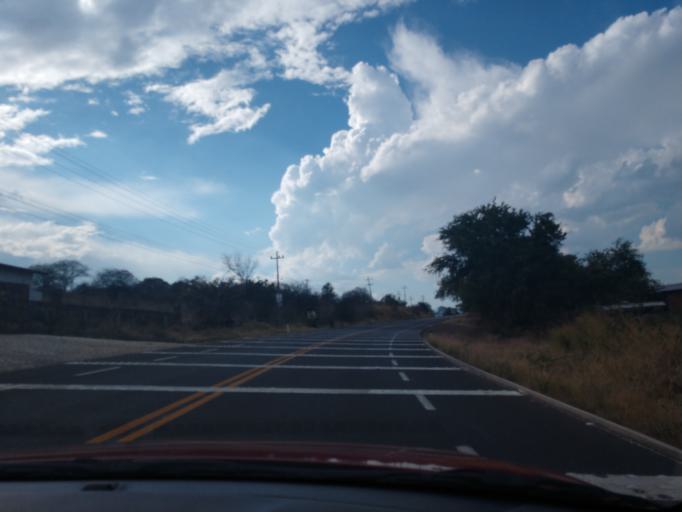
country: MX
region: Jalisco
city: Ajijic
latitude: 20.1873
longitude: -103.2535
